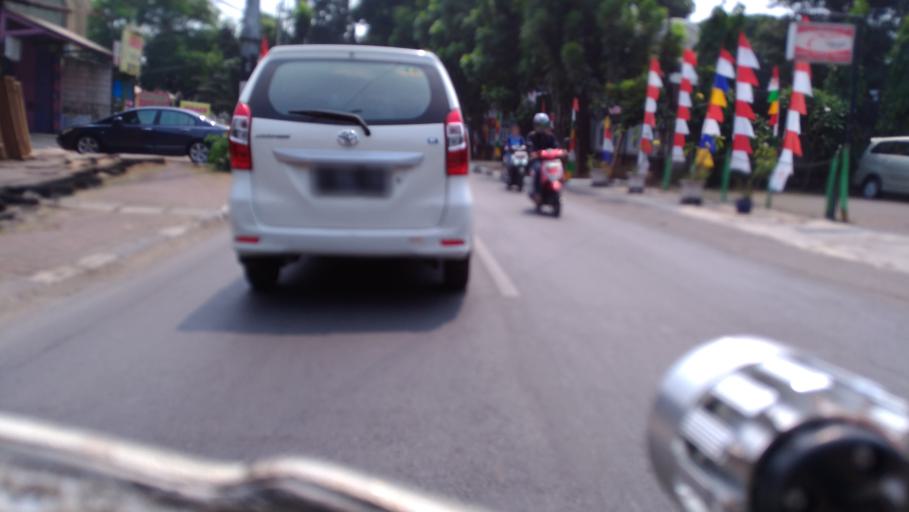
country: ID
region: West Java
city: Cileungsir
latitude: -6.3208
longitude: 106.8896
